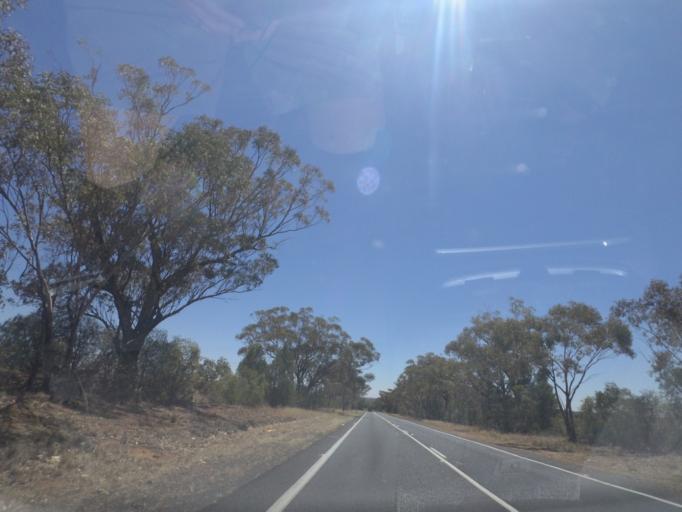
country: AU
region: New South Wales
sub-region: Gilgandra
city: Gilgandra
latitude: -31.4658
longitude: 148.9434
